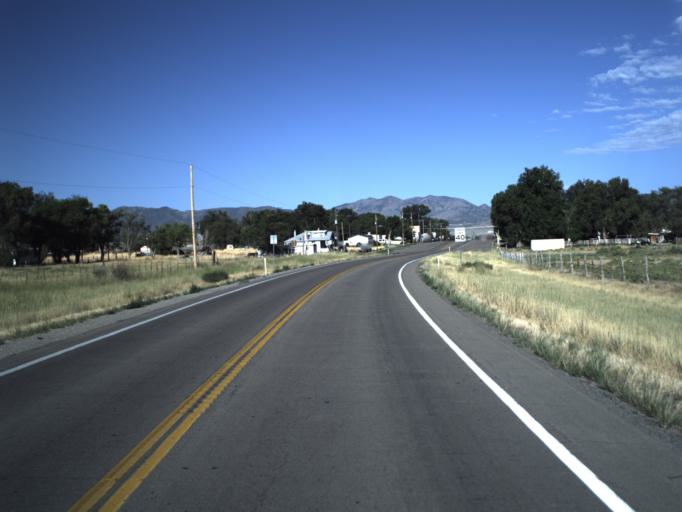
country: US
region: Utah
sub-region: Utah County
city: Genola
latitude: 39.9530
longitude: -111.8949
